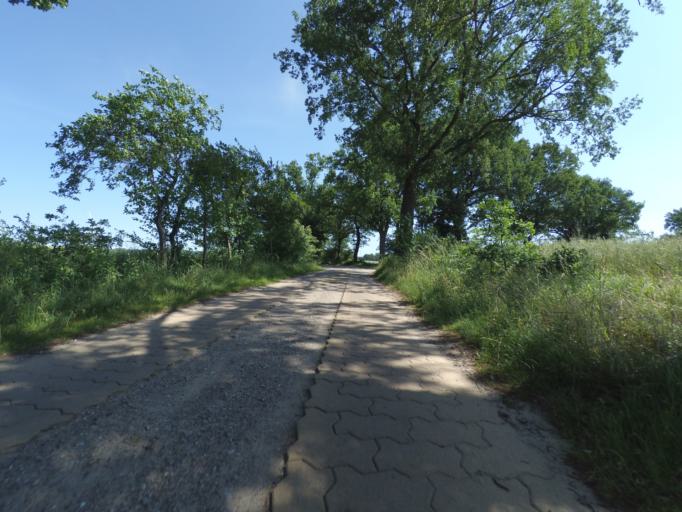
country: DE
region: Brandenburg
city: Pritzwalk
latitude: 53.1230
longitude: 12.2328
